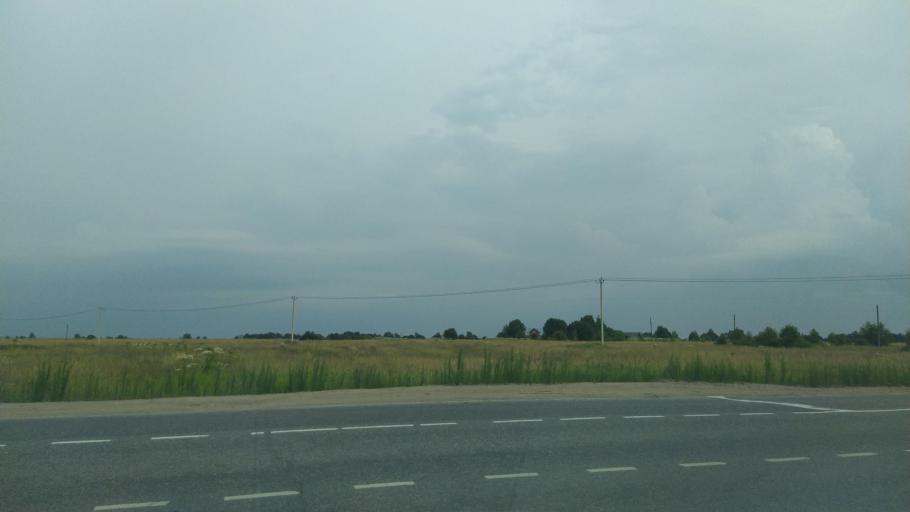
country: RU
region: Leningrad
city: Koltushi
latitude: 59.8904
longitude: 30.7333
